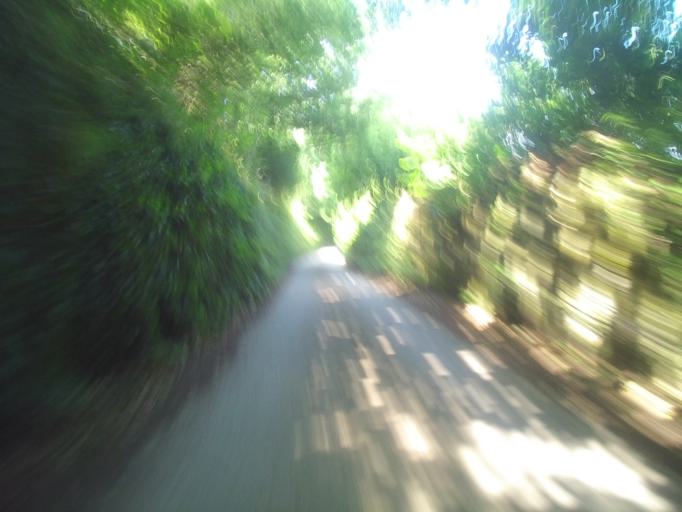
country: GB
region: England
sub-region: Devon
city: Dartmouth
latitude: 50.3539
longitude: -3.5975
